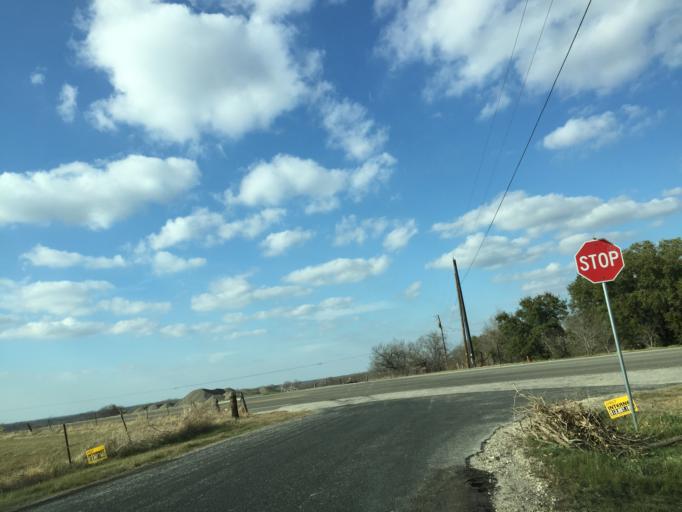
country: US
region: Texas
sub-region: Williamson County
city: Taylor
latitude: 30.6387
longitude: -97.4209
